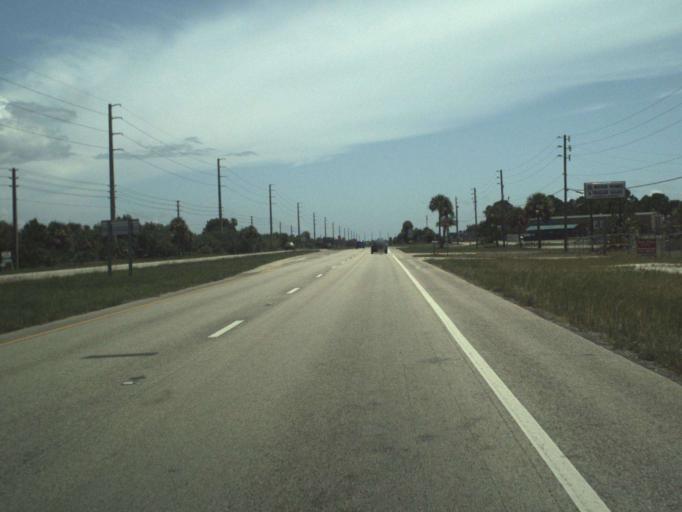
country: US
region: Florida
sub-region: Saint Lucie County
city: Lakewood Park
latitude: 27.5184
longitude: -80.3547
